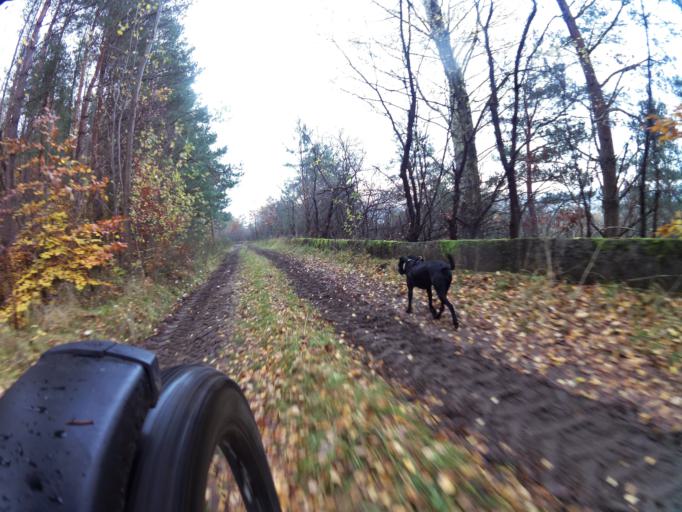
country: PL
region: Pomeranian Voivodeship
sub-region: Powiat pucki
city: Krokowa
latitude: 54.7426
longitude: 18.0991
